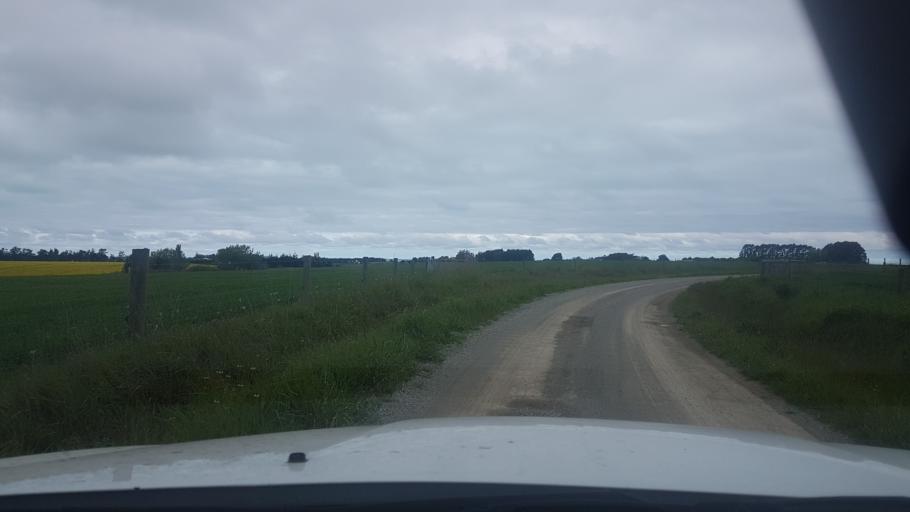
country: NZ
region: Canterbury
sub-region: Timaru District
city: Timaru
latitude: -44.4435
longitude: 171.2049
